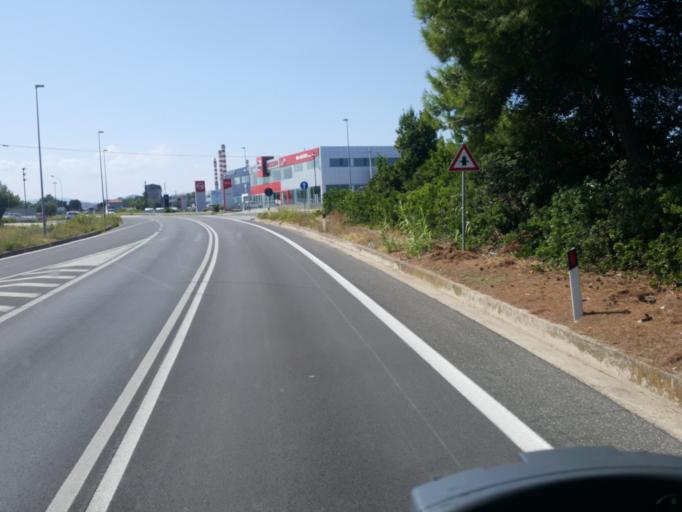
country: IT
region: Abruzzo
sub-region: Provincia di Chieti
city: Salvo Marina
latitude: 42.0603
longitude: 14.7658
